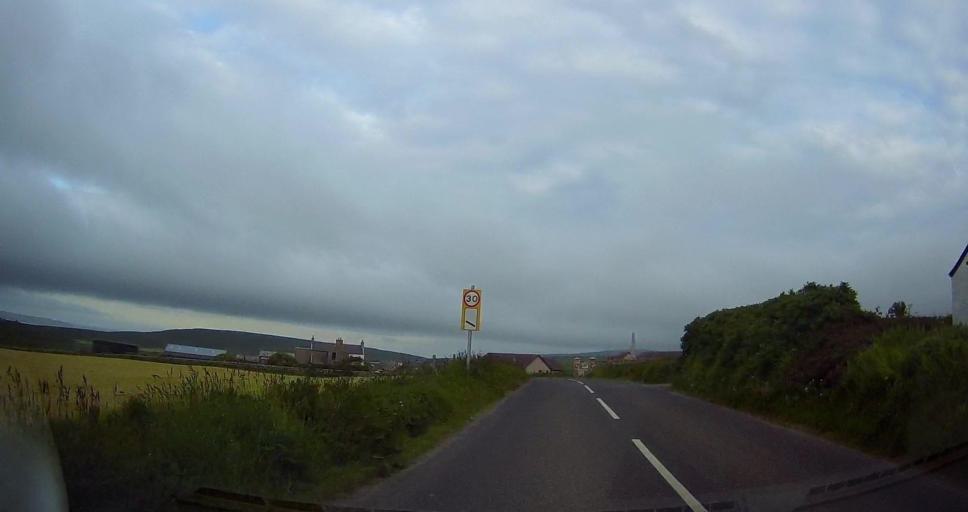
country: GB
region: Scotland
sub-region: Orkney Islands
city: Orkney
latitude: 59.1155
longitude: -3.1139
